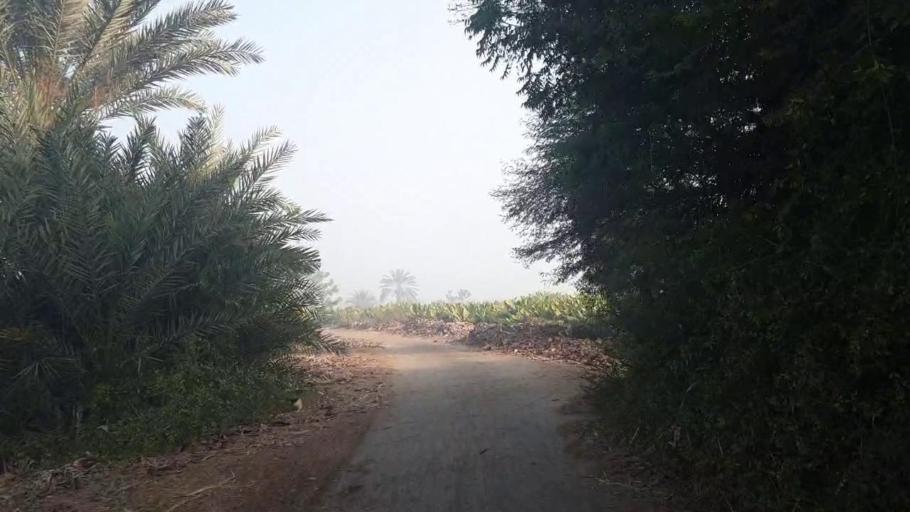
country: PK
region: Sindh
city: Tando Adam
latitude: 25.8034
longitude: 68.6332
